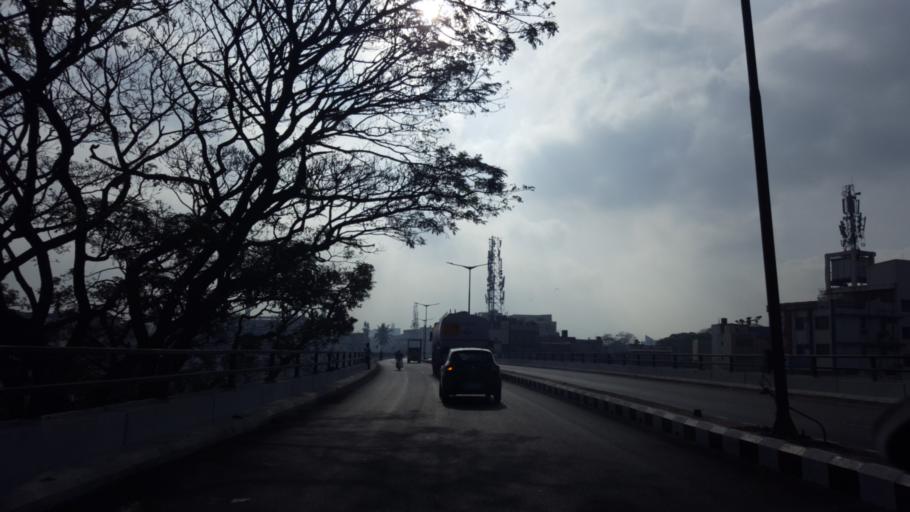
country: IN
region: Karnataka
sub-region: Bangalore Urban
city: Bangalore
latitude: 12.9644
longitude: 77.5763
